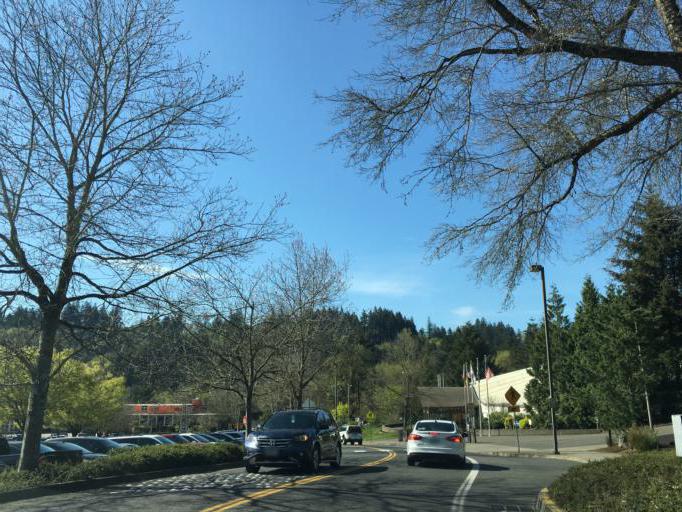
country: US
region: Oregon
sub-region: Multnomah County
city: Portland
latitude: 45.5103
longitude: -122.7177
